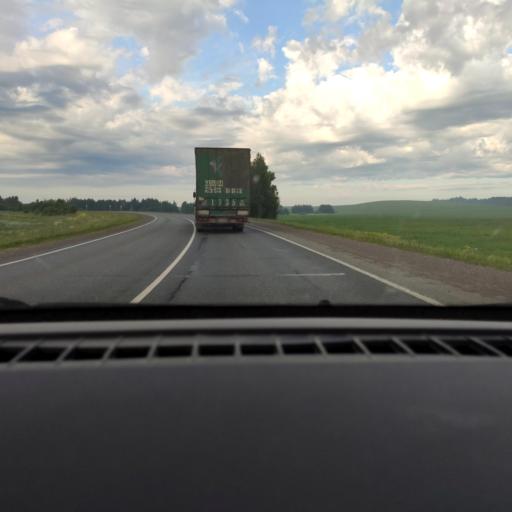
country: RU
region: Perm
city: Chastyye
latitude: 57.3949
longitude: 54.4382
